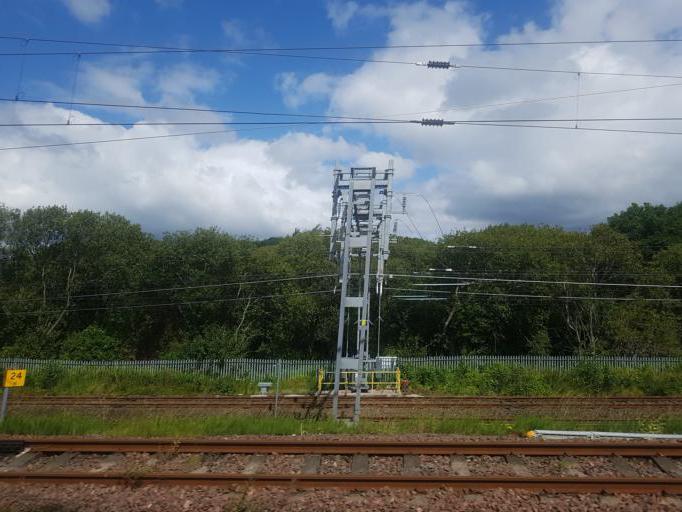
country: GB
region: Scotland
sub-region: Falkirk
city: Polmont
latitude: 55.9856
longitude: -3.7262
